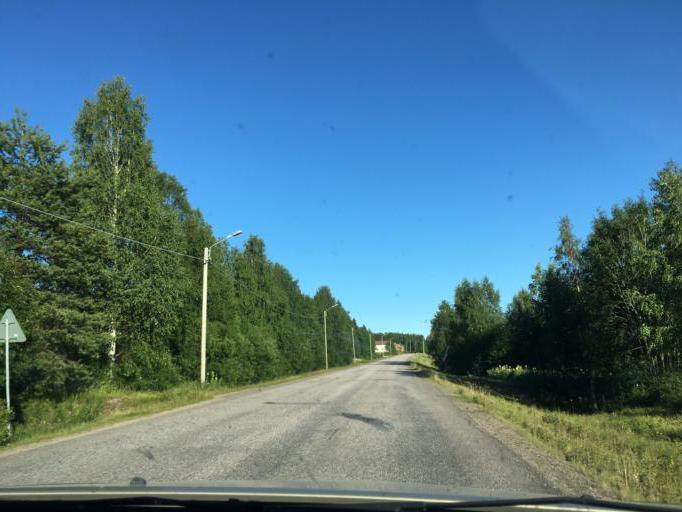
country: SE
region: Norrbotten
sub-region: Kalix Kommun
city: Rolfs
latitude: 65.9255
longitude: 22.9036
